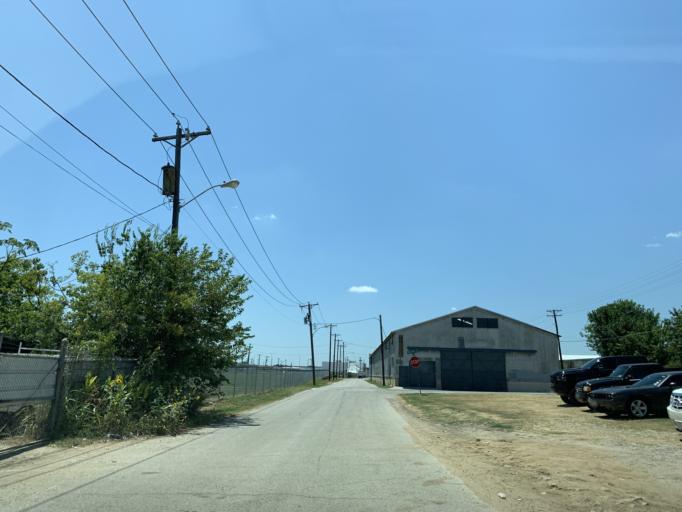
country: US
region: Texas
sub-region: Dallas County
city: Dallas
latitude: 32.7728
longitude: -96.7732
